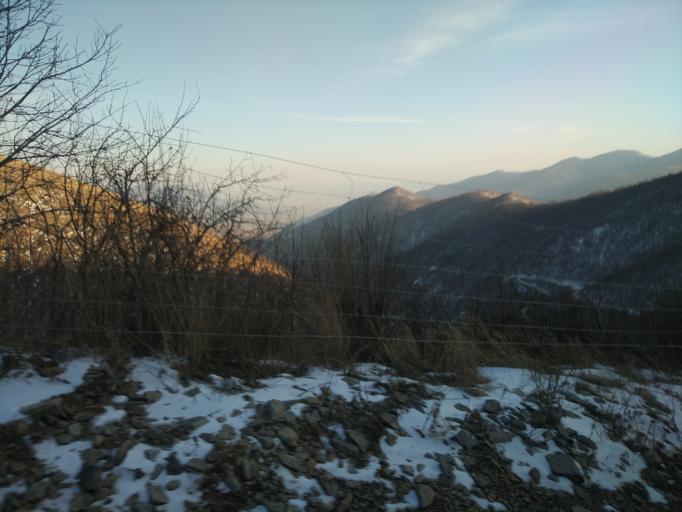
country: CN
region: Hebei
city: Xiwanzi
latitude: 40.8742
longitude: 115.4527
